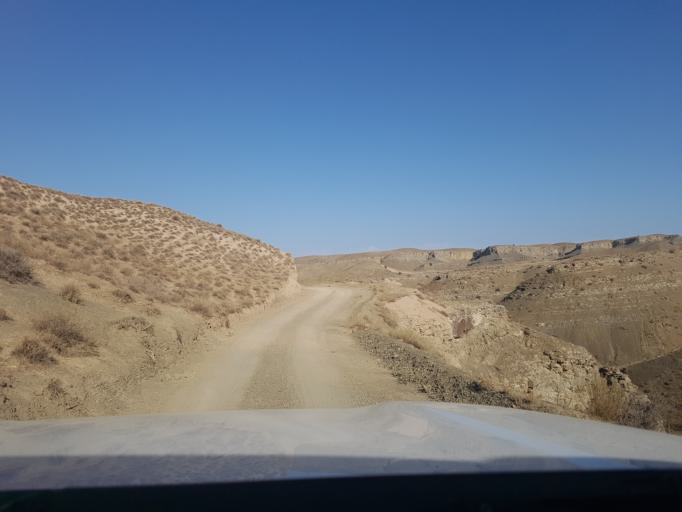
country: TM
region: Balkan
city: Magtymguly
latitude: 38.3006
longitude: 56.7825
